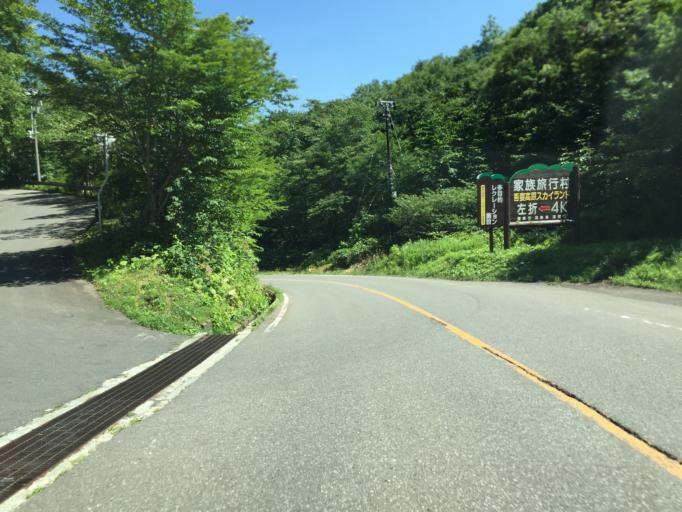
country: JP
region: Fukushima
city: Fukushima-shi
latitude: 37.7534
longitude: 140.3111
